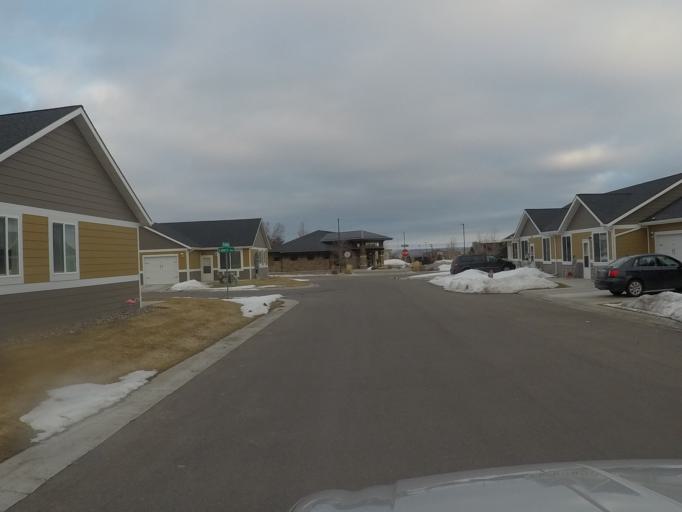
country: US
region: Montana
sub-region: Yellowstone County
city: Billings
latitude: 45.7860
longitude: -108.6217
